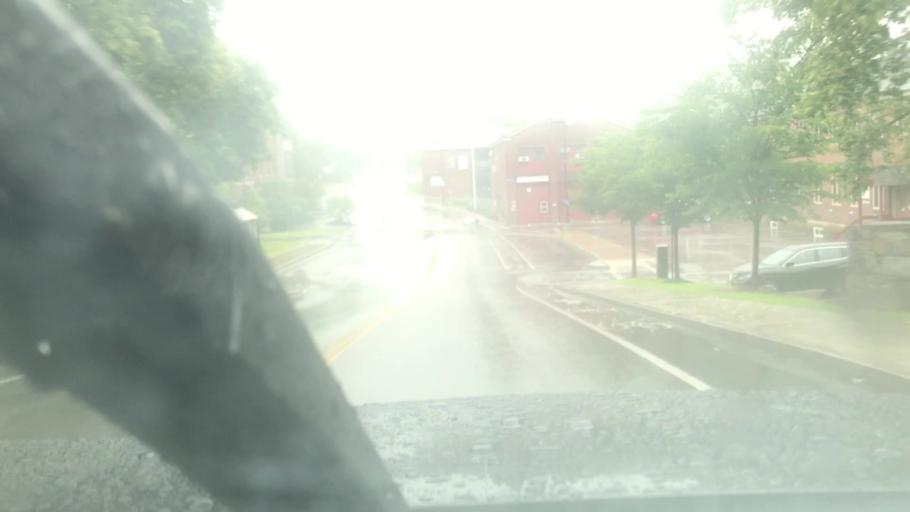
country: US
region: New Hampshire
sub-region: Strafford County
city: Durham
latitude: 43.1366
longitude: -70.9354
